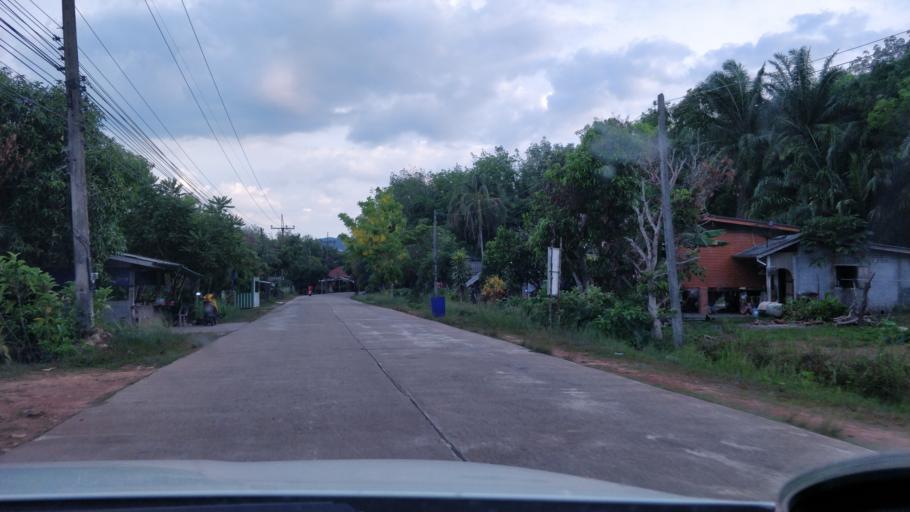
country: TH
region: Krabi
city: Saladan
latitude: 7.5881
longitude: 99.0688
